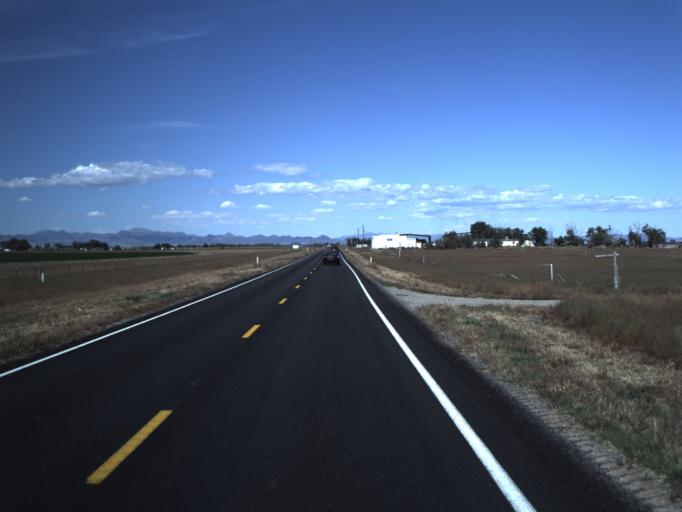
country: US
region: Utah
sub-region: Washington County
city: Enterprise
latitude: 37.6810
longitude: -113.6565
